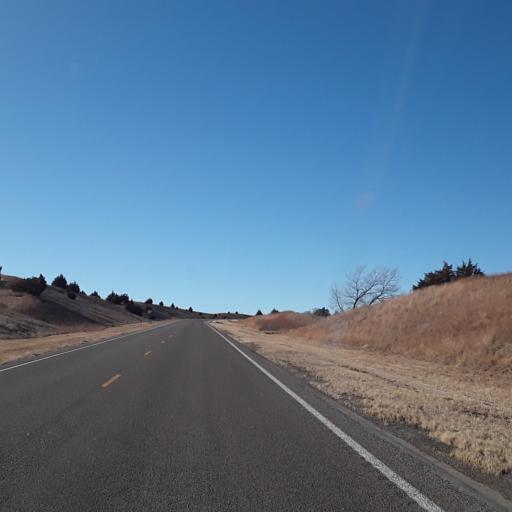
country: US
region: Nebraska
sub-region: Frontier County
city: Stockville
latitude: 40.6320
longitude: -100.5786
